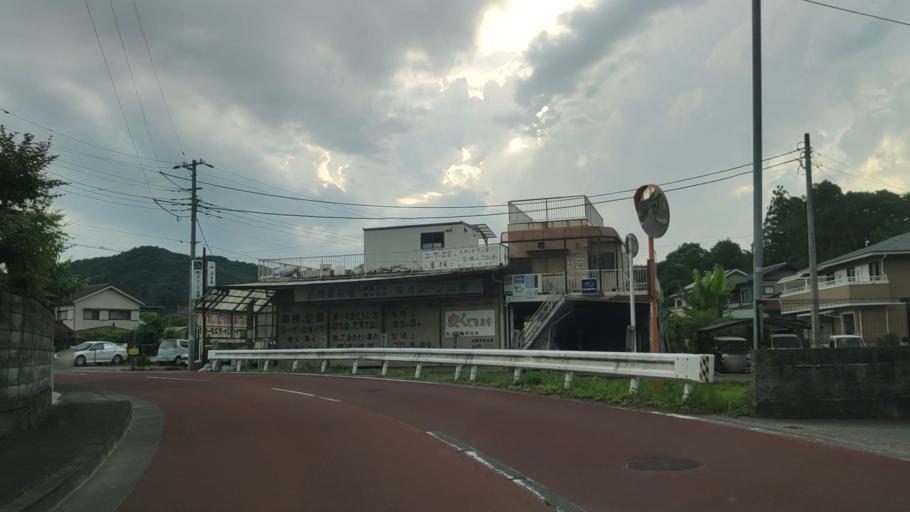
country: JP
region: Saitama
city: Hanno
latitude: 35.8341
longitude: 139.2987
